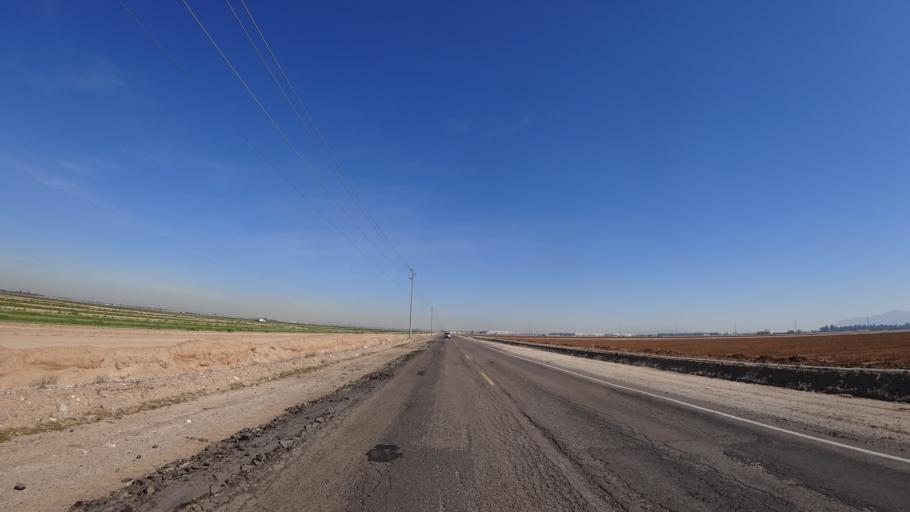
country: US
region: Arizona
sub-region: Maricopa County
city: Citrus Park
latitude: 33.5082
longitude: -112.4414
